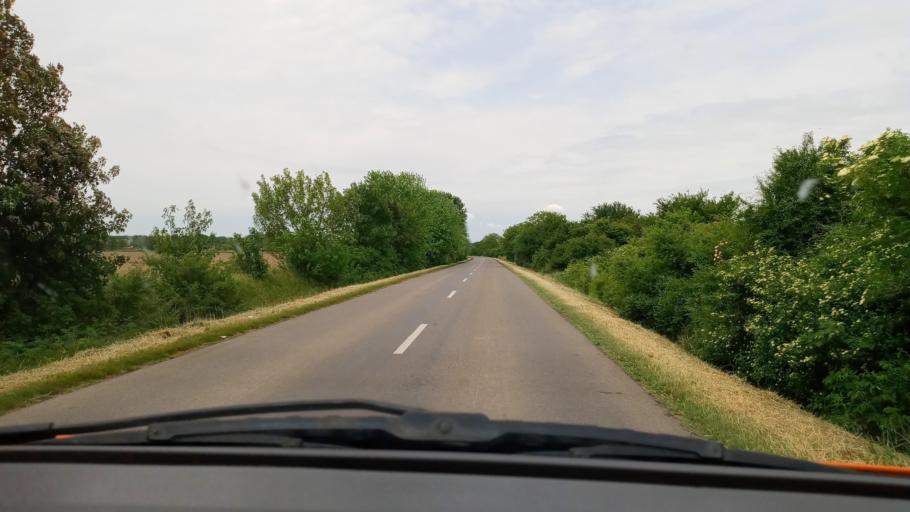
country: HU
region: Baranya
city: Vajszlo
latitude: 45.8929
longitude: 18.0199
